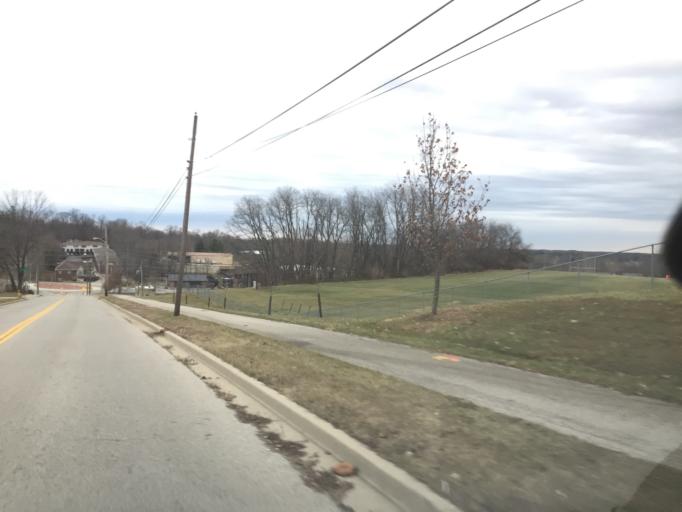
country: US
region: Indiana
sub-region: Monroe County
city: Bloomington
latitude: 39.1766
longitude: -86.5471
